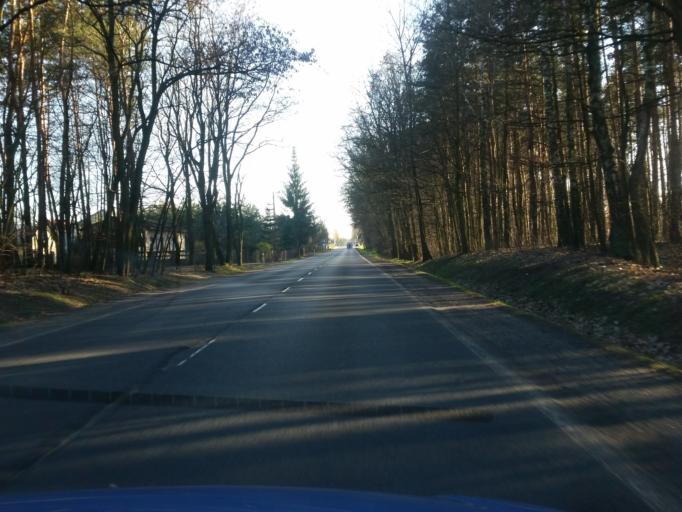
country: PL
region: Lodz Voivodeship
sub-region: Powiat radomszczanski
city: Gomunice
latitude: 51.1650
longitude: 19.4925
